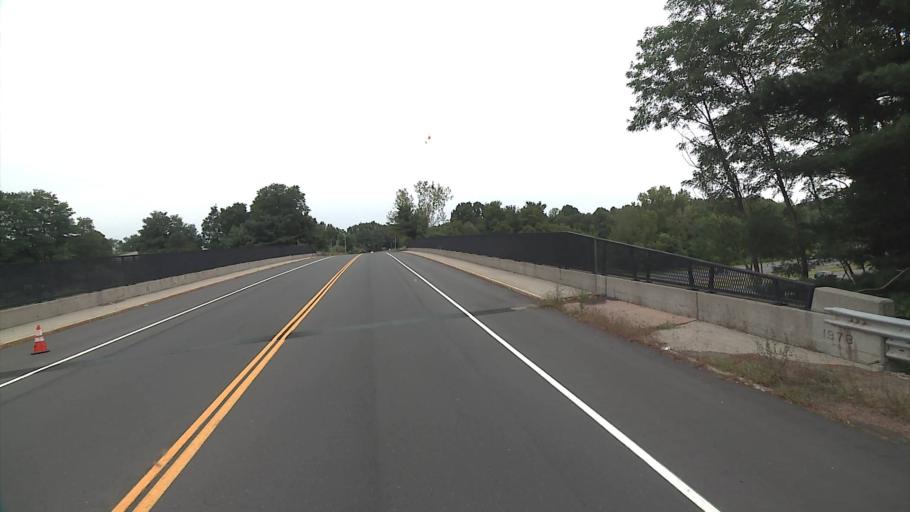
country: US
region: Connecticut
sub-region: Tolland County
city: Rockville
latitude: 41.8320
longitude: -72.4664
